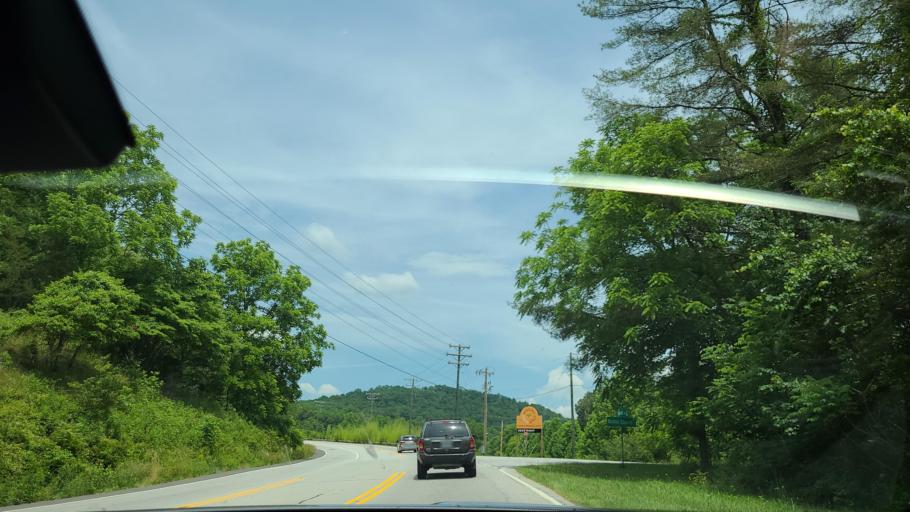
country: US
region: North Carolina
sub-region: Macon County
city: Franklin
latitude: 35.1737
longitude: -83.3406
